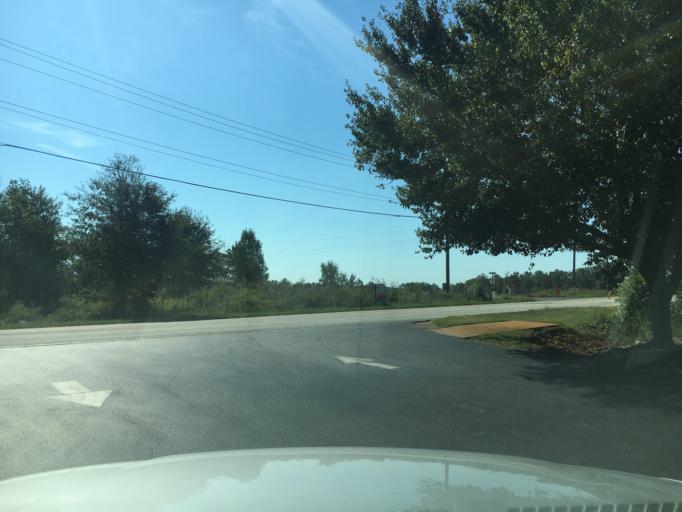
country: US
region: South Carolina
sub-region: Greenville County
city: Taylors
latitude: 34.9163
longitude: -82.2674
